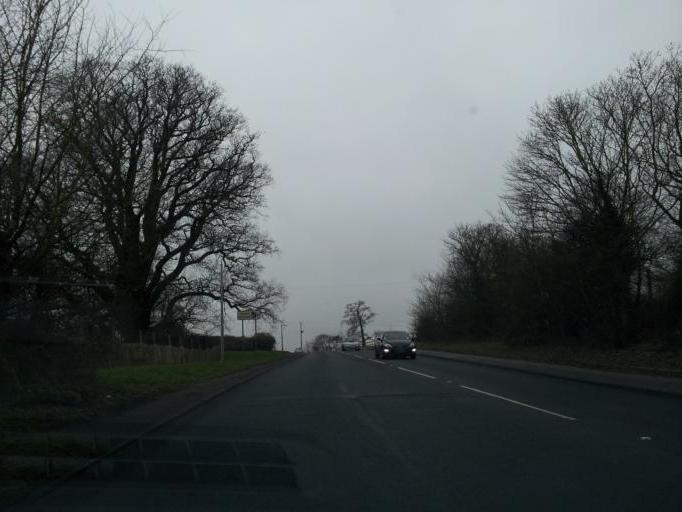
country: GB
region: England
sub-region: Essex
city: Manningtree
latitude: 51.9436
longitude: 1.0472
